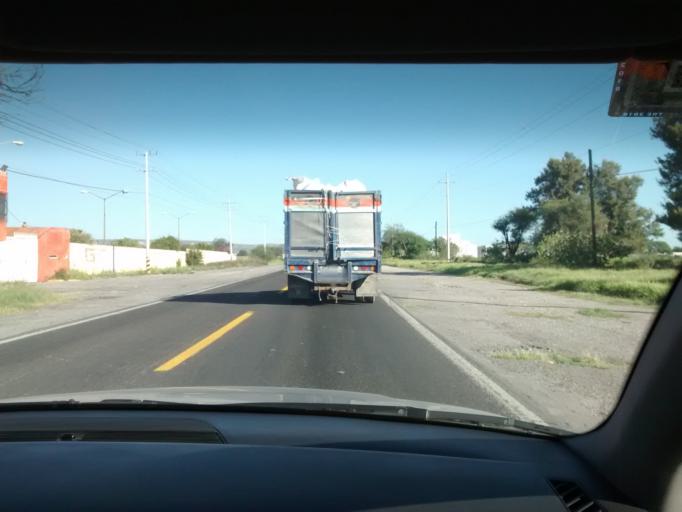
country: MX
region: Puebla
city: San Bartolo Teontepec
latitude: 18.5381
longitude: -97.5329
